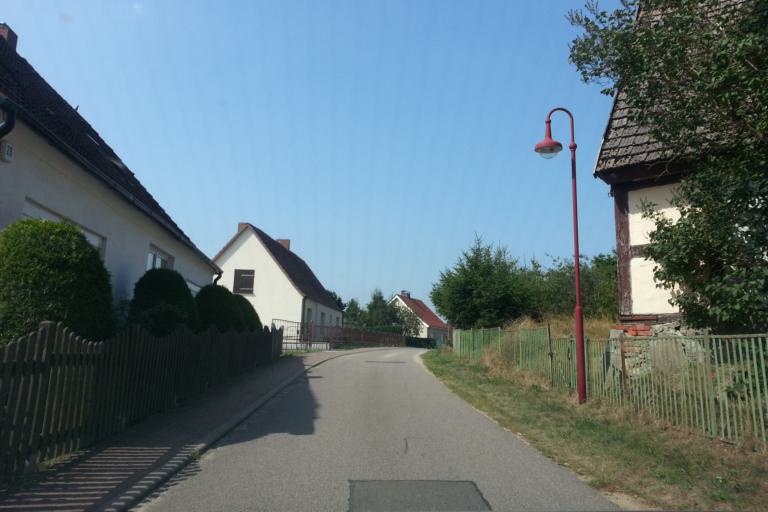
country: DE
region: Mecklenburg-Vorpommern
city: Ferdinandshof
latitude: 53.5922
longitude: 13.8257
